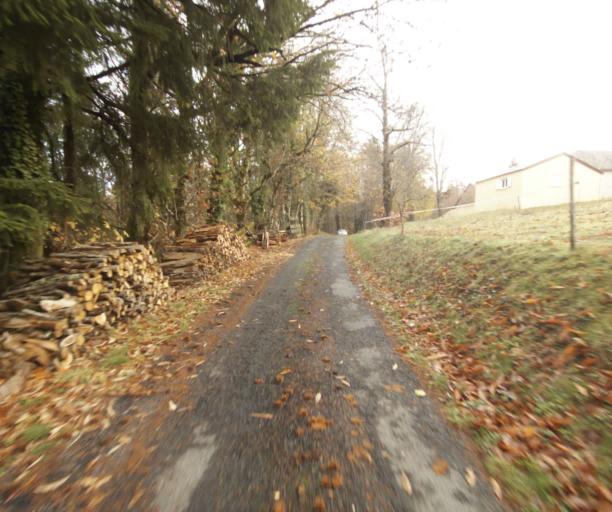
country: FR
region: Limousin
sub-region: Departement de la Correze
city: Cornil
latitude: 45.2056
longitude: 1.7211
